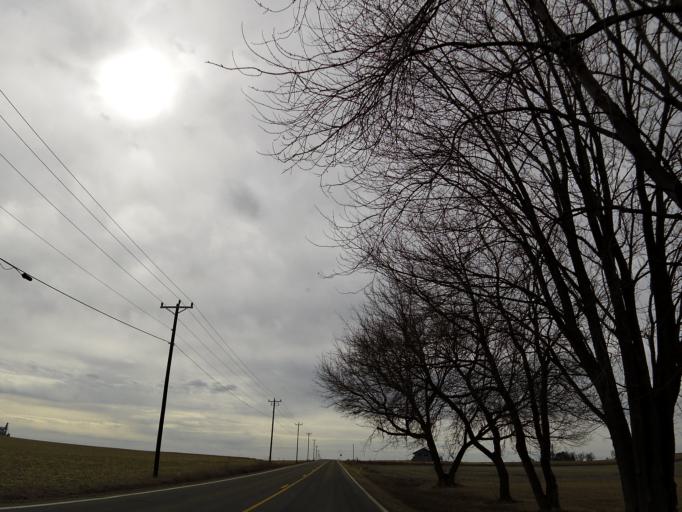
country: US
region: Minnesota
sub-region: Washington County
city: Afton
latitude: 44.8531
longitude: -92.8422
